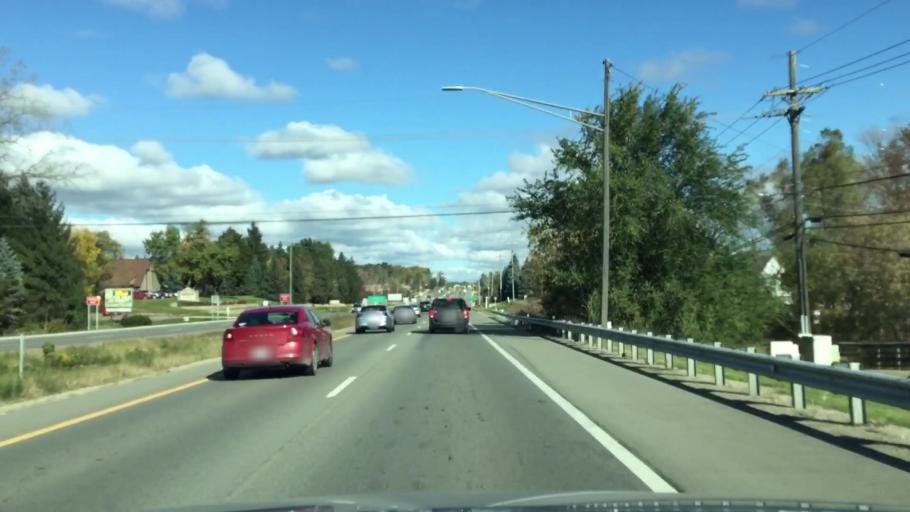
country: US
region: Michigan
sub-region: Oakland County
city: Lake Orion
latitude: 42.7358
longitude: -83.2447
